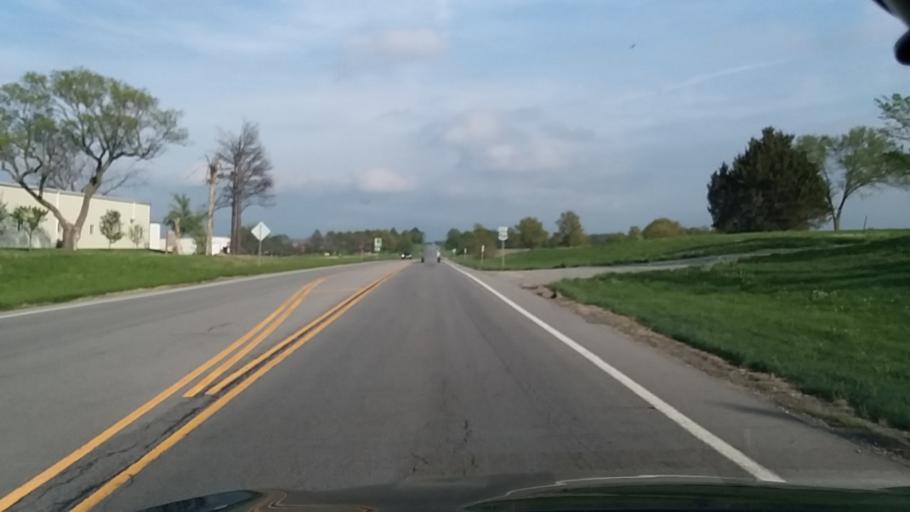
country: US
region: Kansas
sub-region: Douglas County
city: Baldwin City
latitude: 38.7743
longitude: -95.1649
